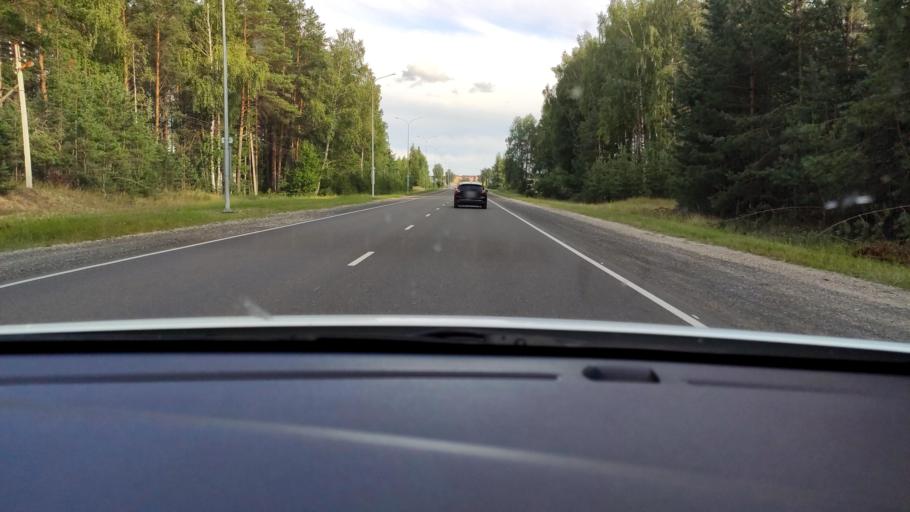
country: RU
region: Mariy-El
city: Surok
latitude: 56.3867
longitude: 48.1915
